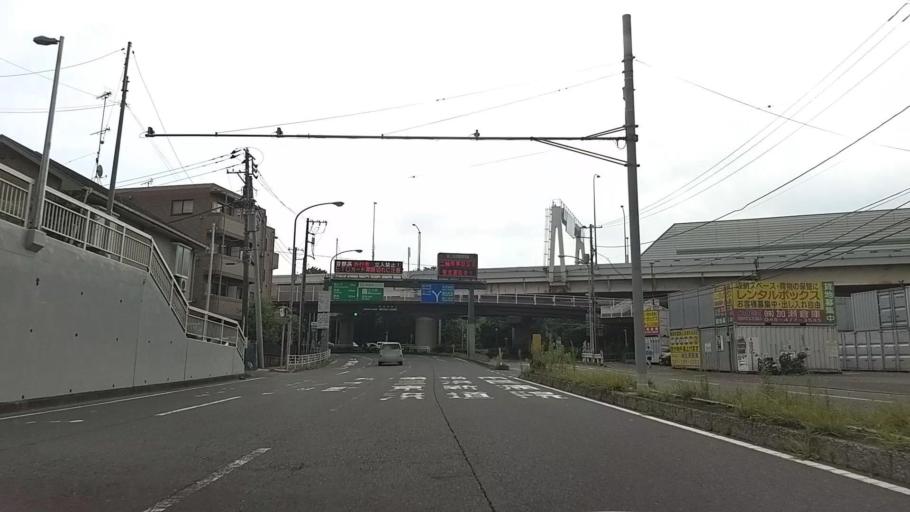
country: JP
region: Kanagawa
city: Yokohama
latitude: 35.4736
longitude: 139.6029
